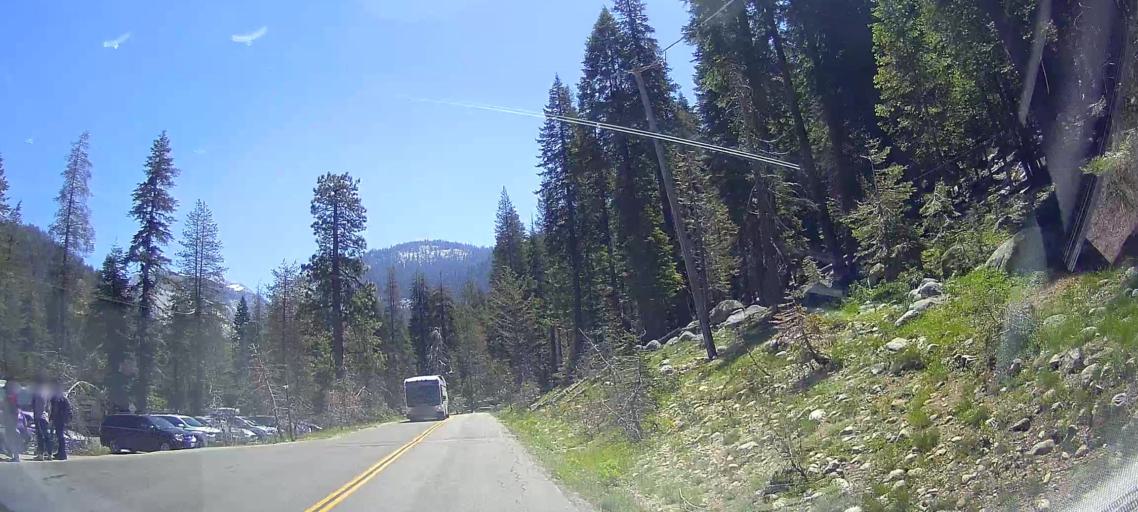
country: US
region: California
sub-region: Tulare County
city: Three Rivers
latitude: 36.6039
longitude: -118.7318
